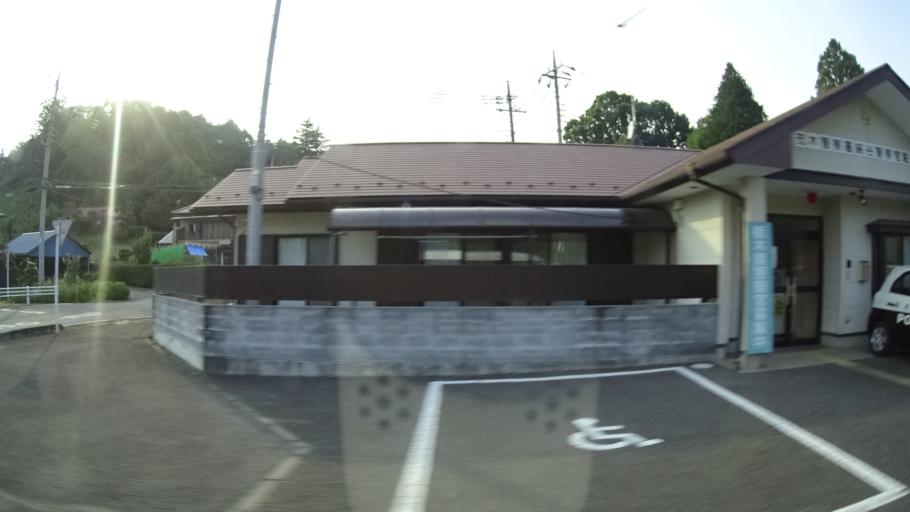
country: JP
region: Tochigi
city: Karasuyama
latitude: 36.5852
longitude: 140.1132
